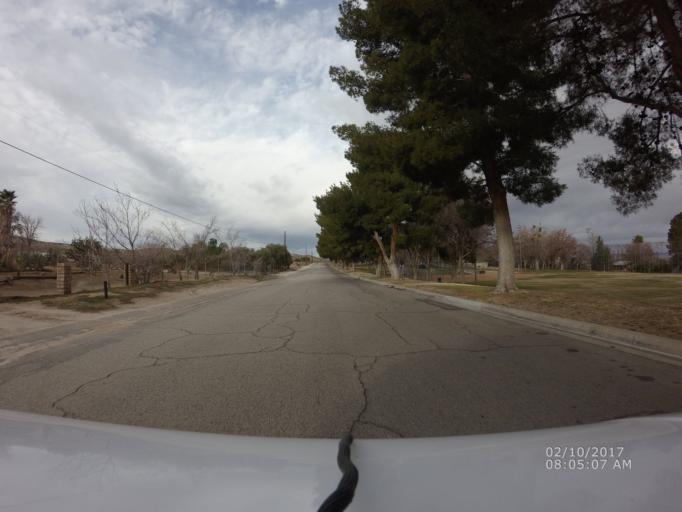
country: US
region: California
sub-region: Los Angeles County
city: Littlerock
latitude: 34.5010
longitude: -117.9112
